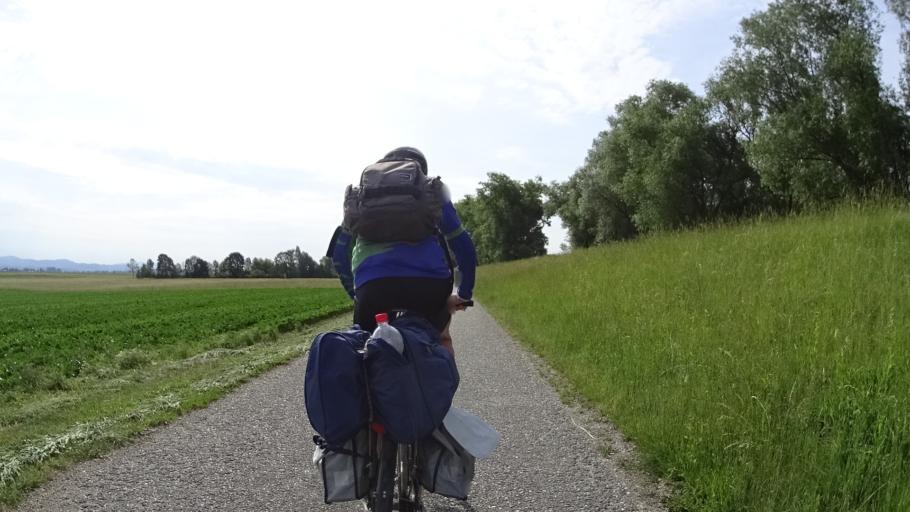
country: DE
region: Bavaria
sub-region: Lower Bavaria
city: Mariaposching
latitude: 48.8306
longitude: 12.7879
